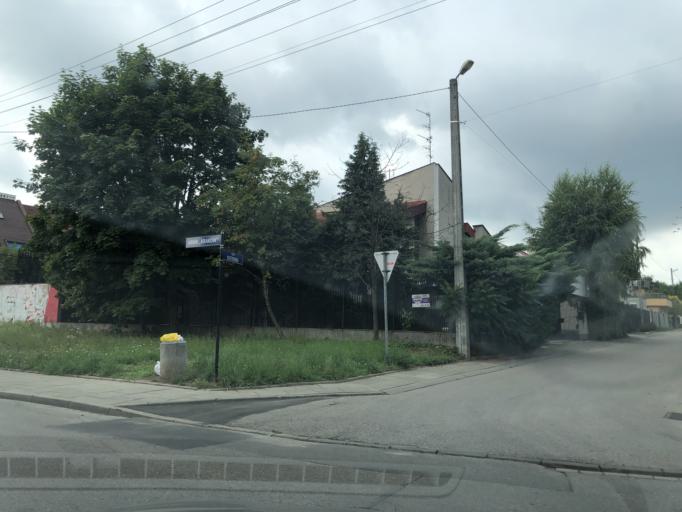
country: PL
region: Lesser Poland Voivodeship
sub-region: Powiat krakowski
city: Libertow
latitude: 50.0041
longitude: 19.9265
